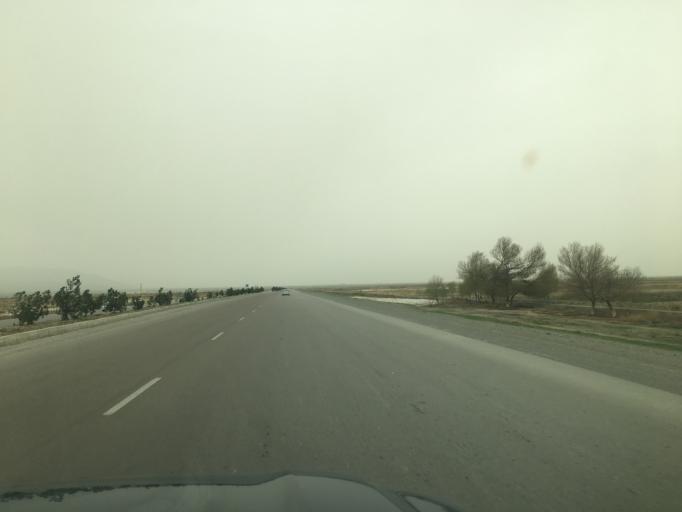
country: TM
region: Ahal
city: Baharly
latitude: 38.3592
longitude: 57.5351
